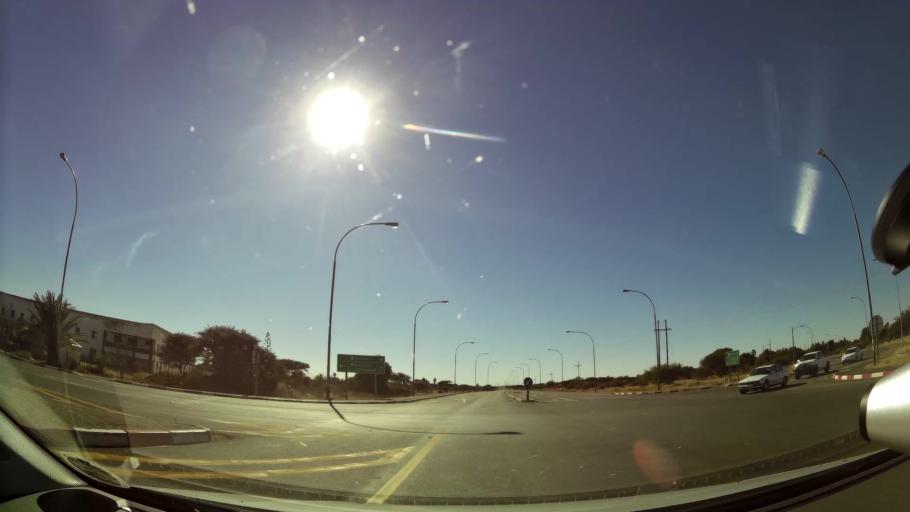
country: ZA
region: Northern Cape
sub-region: Frances Baard District Municipality
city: Warrenton
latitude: -28.1126
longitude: 24.8538
